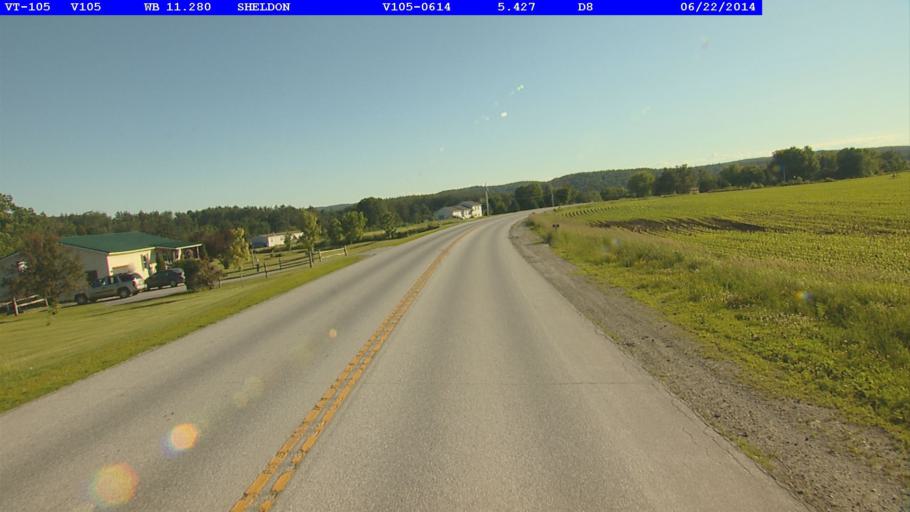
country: US
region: Vermont
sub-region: Franklin County
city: Enosburg Falls
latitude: 44.9032
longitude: -72.9275
